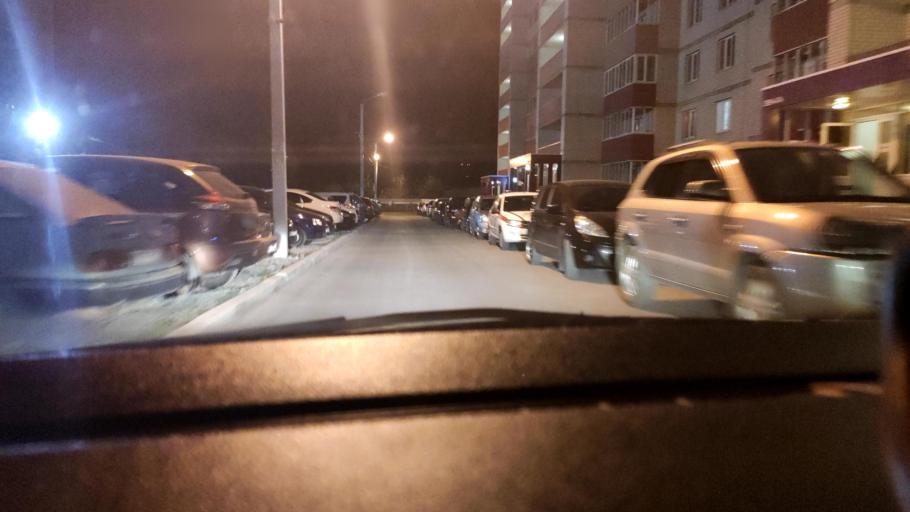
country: RU
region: Voronezj
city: Voronezh
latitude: 51.7133
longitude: 39.1998
